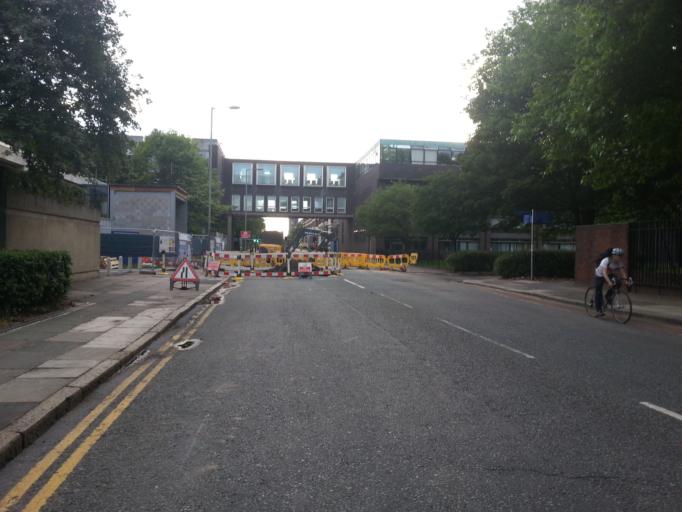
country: GB
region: England
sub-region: Liverpool
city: Liverpool
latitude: 53.4032
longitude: -2.9625
